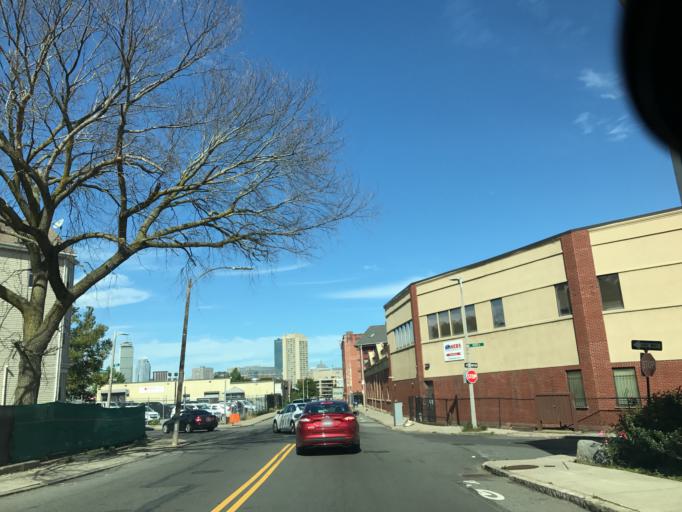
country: US
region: Massachusetts
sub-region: Suffolk County
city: South Boston
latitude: 42.3267
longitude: -71.0752
